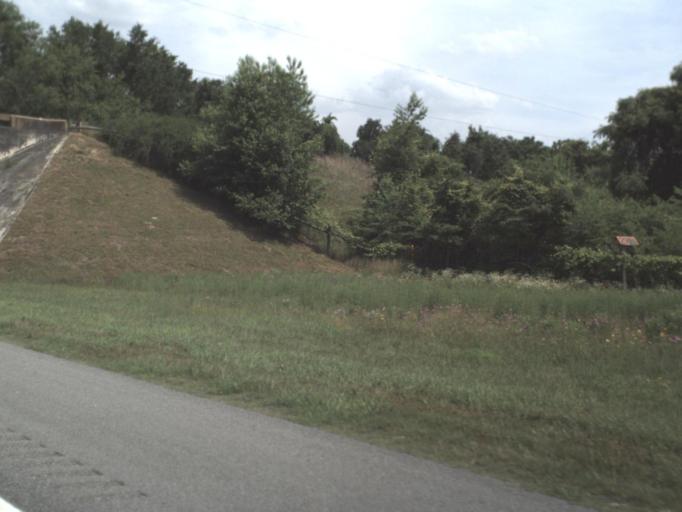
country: US
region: Florida
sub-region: Suwannee County
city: Live Oak
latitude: 30.3517
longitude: -83.0273
